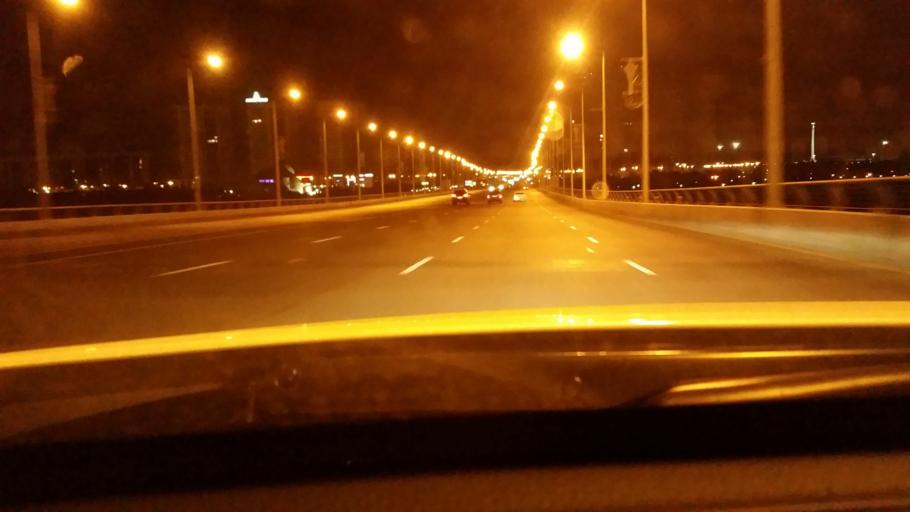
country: KZ
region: Astana Qalasy
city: Astana
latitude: 51.1308
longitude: 71.4494
